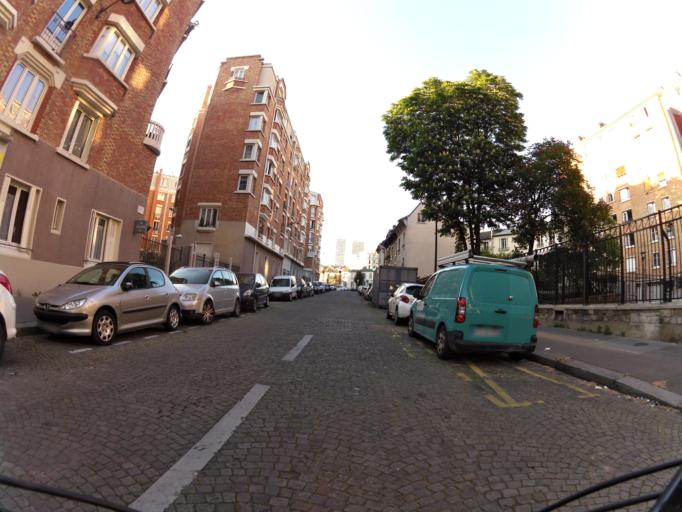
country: FR
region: Ile-de-France
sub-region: Departement du Val-de-Marne
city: Le Kremlin-Bicetre
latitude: 48.8223
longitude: 2.3541
